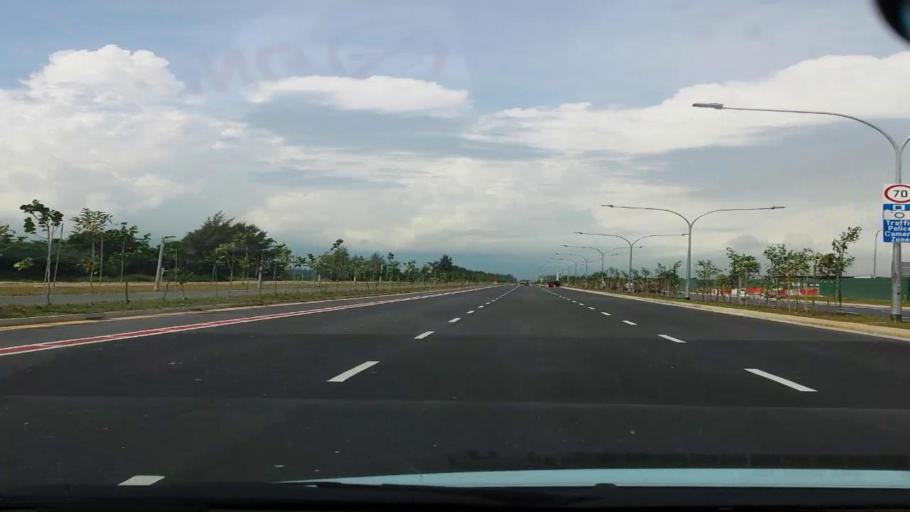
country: SG
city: Singapore
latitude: 1.3496
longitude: 104.0289
